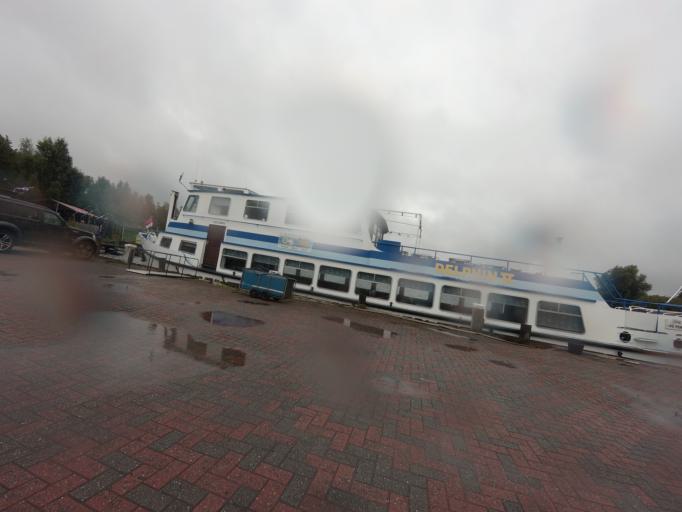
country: NL
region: Friesland
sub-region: Gemeente Tytsjerksteradiel
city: Garyp
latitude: 53.1350
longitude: 5.9533
